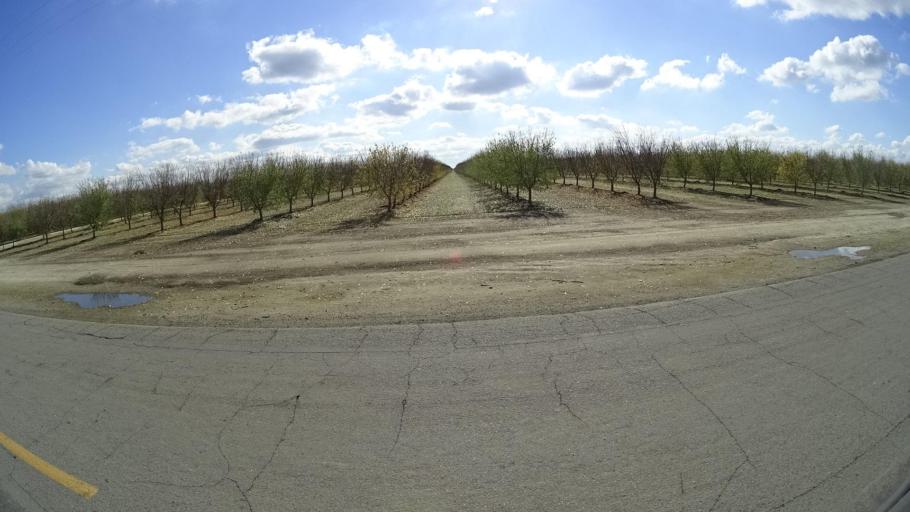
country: US
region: California
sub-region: Kern County
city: Delano
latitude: 35.7322
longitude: -119.3440
